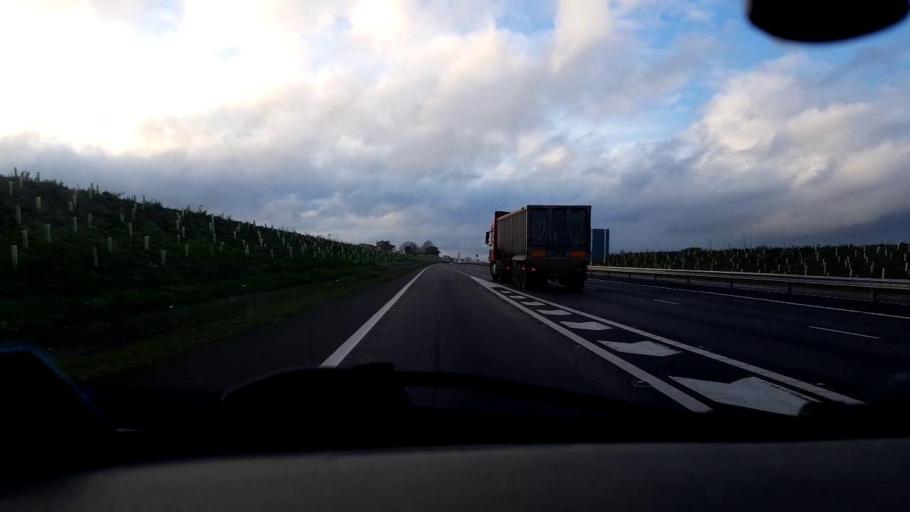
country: GB
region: England
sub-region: Norfolk
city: Horsford
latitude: 52.6820
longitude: 1.2560
